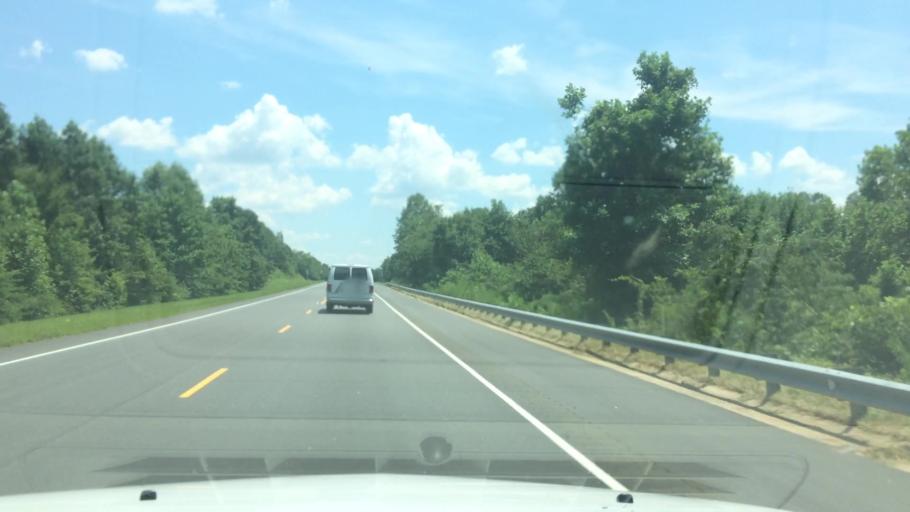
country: US
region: North Carolina
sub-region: Alexander County
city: Stony Point
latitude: 35.8206
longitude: -81.0058
